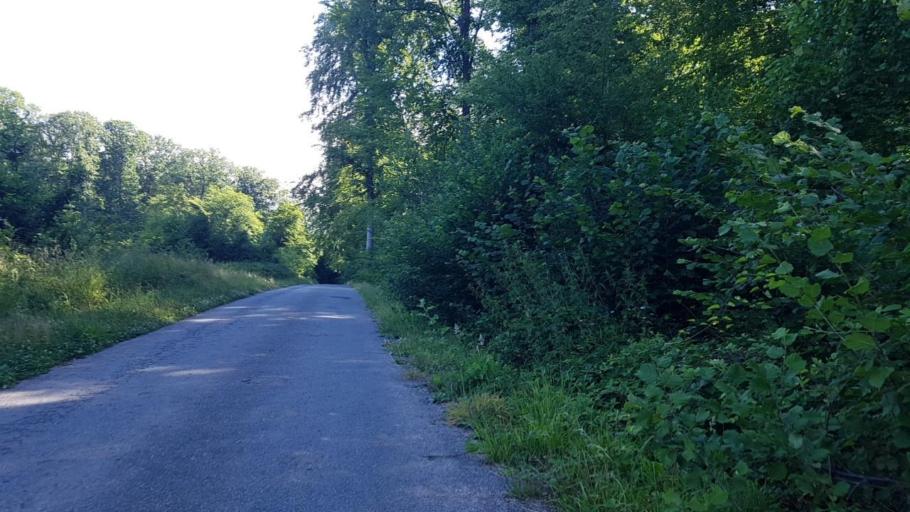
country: FR
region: Picardie
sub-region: Departement de l'Oise
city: Fleurines
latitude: 49.2548
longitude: 2.6184
